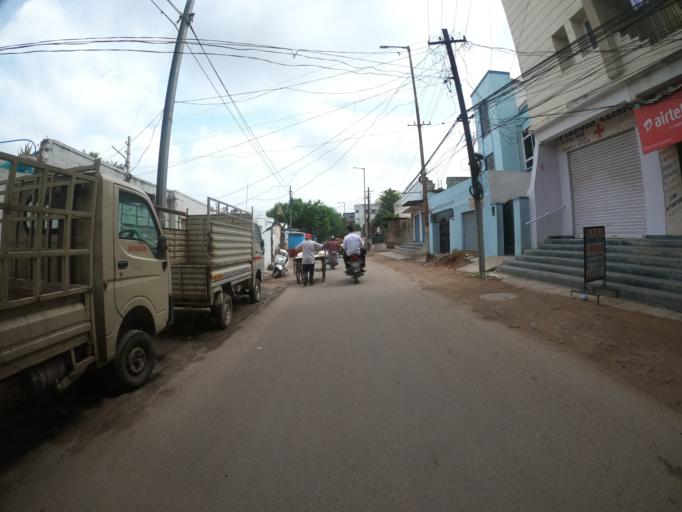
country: IN
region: Telangana
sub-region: Hyderabad
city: Hyderabad
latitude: 17.3937
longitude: 78.4174
